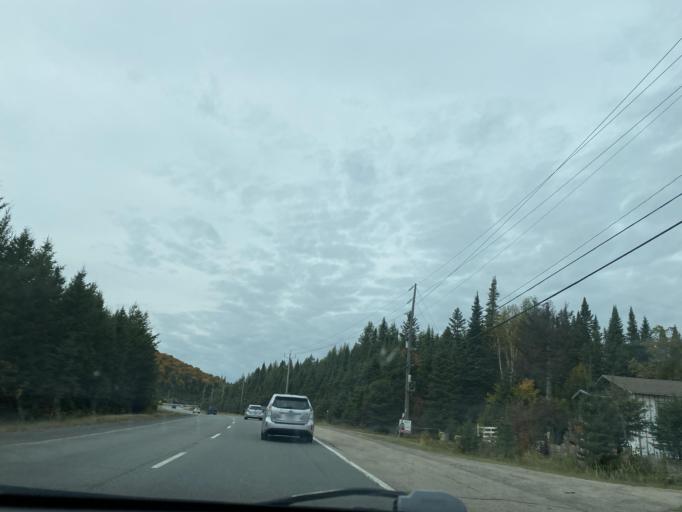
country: CA
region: Quebec
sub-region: Laurentides
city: Sainte-Agathe-des-Monts
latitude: 46.1040
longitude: -74.3879
